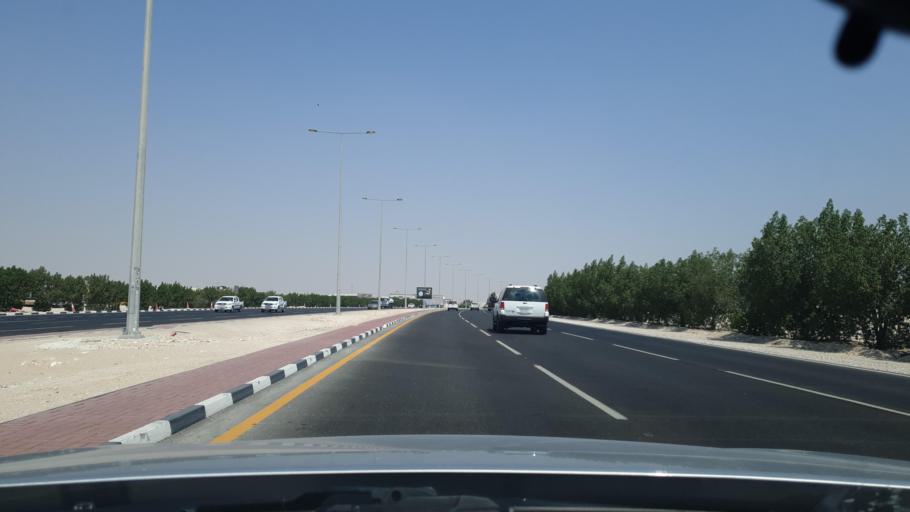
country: QA
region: Al Khawr
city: Al Khawr
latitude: 25.7082
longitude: 51.5054
